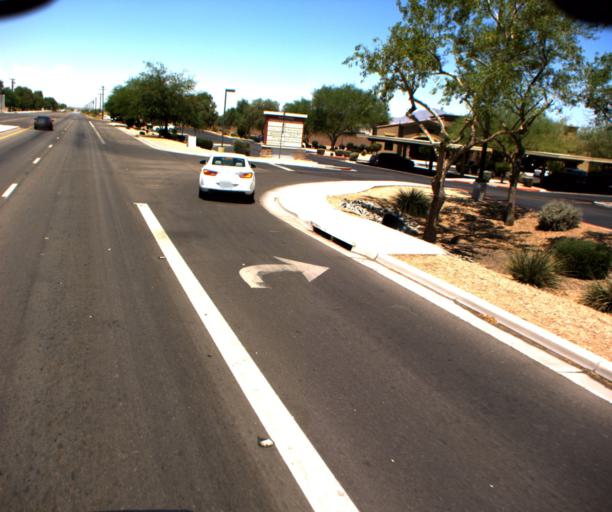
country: US
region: Arizona
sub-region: Pinal County
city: Maricopa
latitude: 33.0725
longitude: -112.0456
